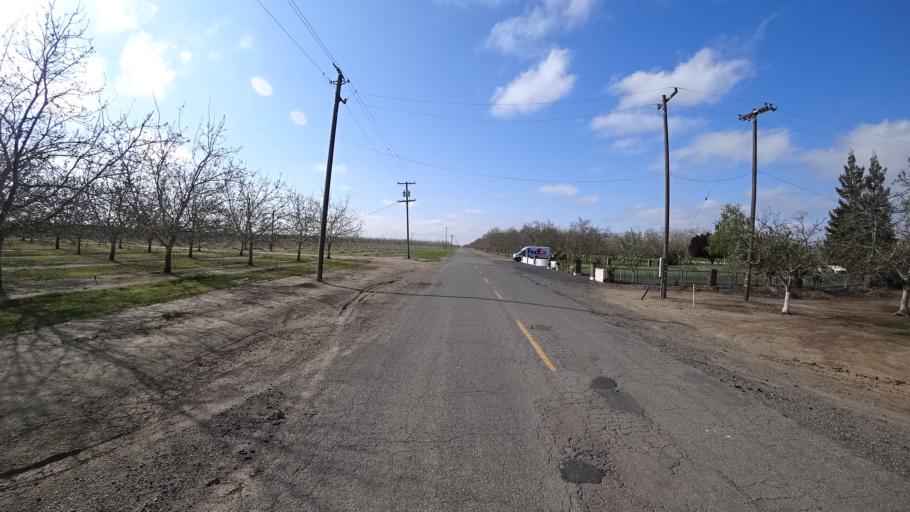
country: US
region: California
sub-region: Glenn County
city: Willows
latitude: 39.4847
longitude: -121.9677
